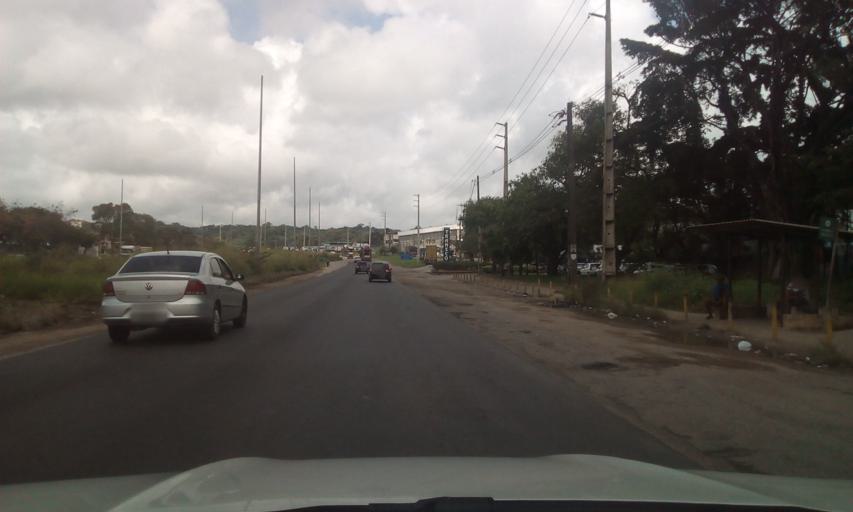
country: BR
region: Pernambuco
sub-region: Paulista
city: Paulista
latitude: -7.9875
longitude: -34.9339
